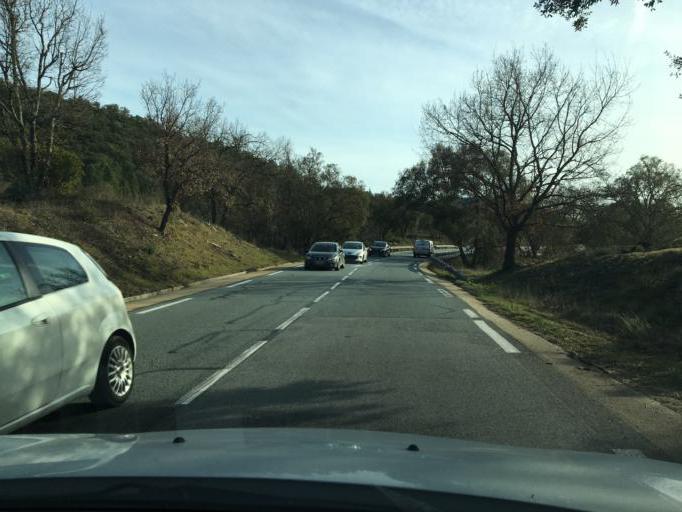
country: FR
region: Provence-Alpes-Cote d'Azur
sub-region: Departement du Var
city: Montauroux
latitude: 43.5592
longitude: 6.7984
